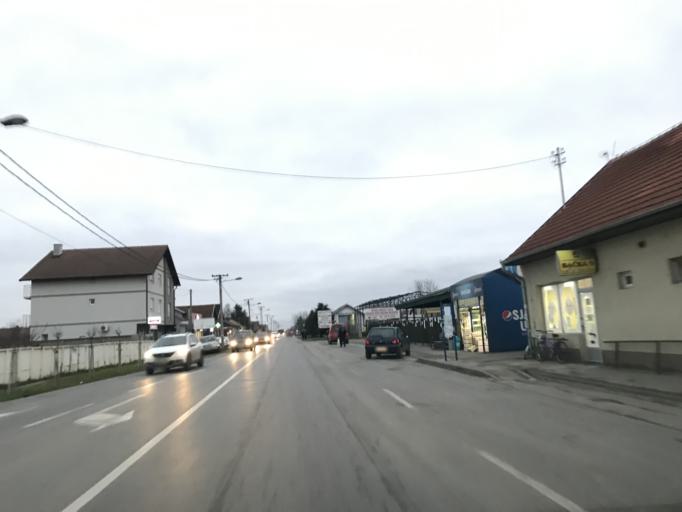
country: RS
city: Rumenka
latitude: 45.2916
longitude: 19.7445
